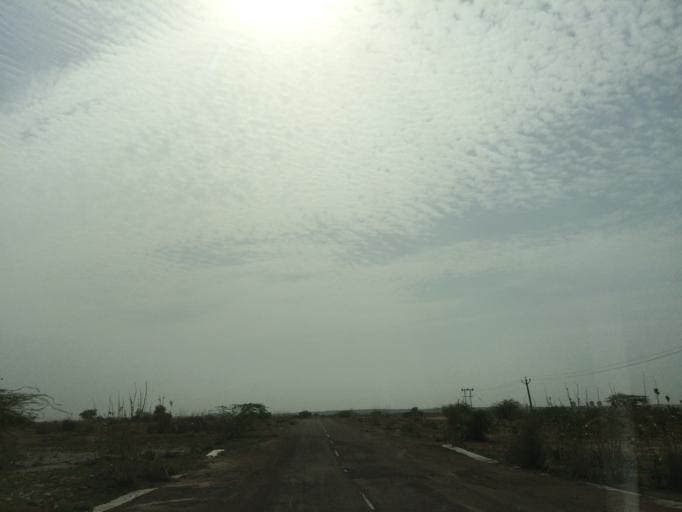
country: IN
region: Rajasthan
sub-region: Jaisalmer
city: Jaisalmer
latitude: 26.8757
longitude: 70.8874
